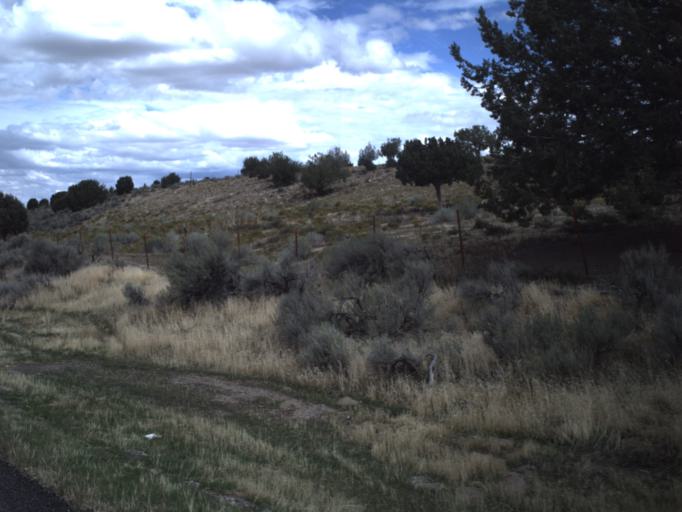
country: US
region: Utah
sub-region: Millard County
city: Fillmore
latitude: 38.9964
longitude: -112.4131
